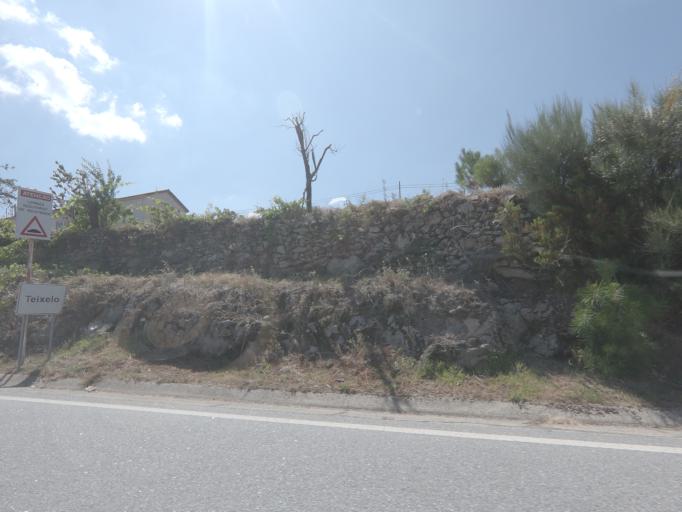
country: PT
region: Viseu
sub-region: Tarouca
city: Tarouca
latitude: 40.9899
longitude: -7.7803
